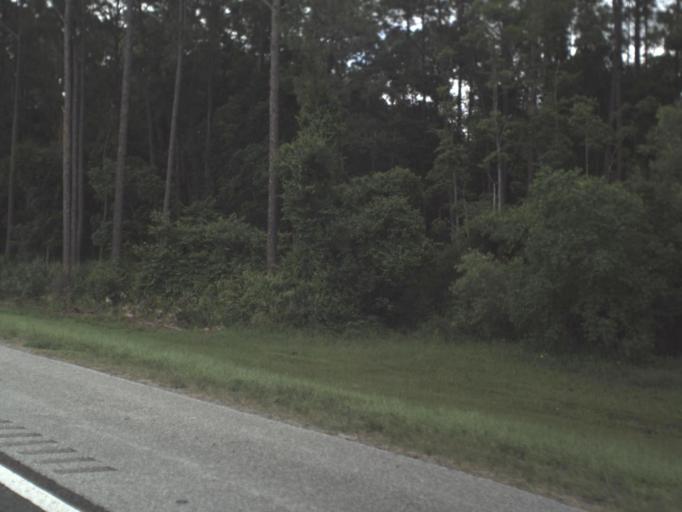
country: US
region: Florida
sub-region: Saint Johns County
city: Saint Augustine Shores
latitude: 29.8107
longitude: -81.3717
